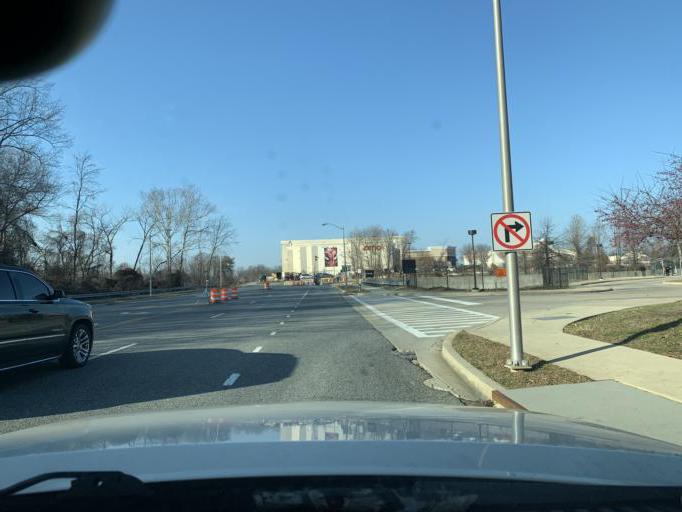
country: US
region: Maryland
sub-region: Prince George's County
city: Largo
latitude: 38.8992
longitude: -76.8466
